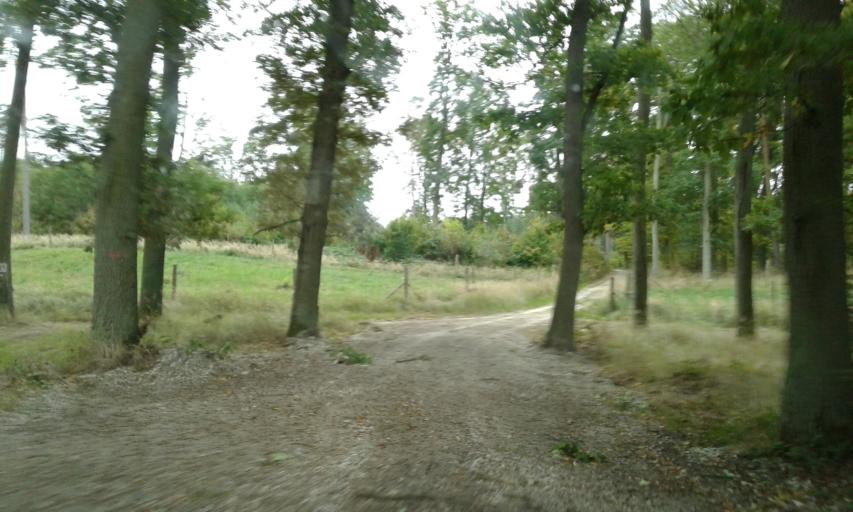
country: PL
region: West Pomeranian Voivodeship
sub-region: Powiat choszczenski
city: Pelczyce
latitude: 53.0874
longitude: 15.2510
